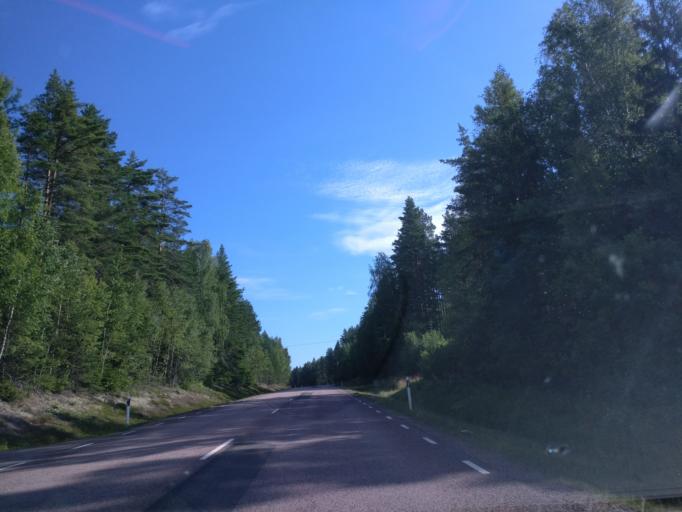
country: SE
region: Vaermland
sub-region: Hagfors Kommun
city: Hagfors
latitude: 60.0589
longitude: 13.7108
